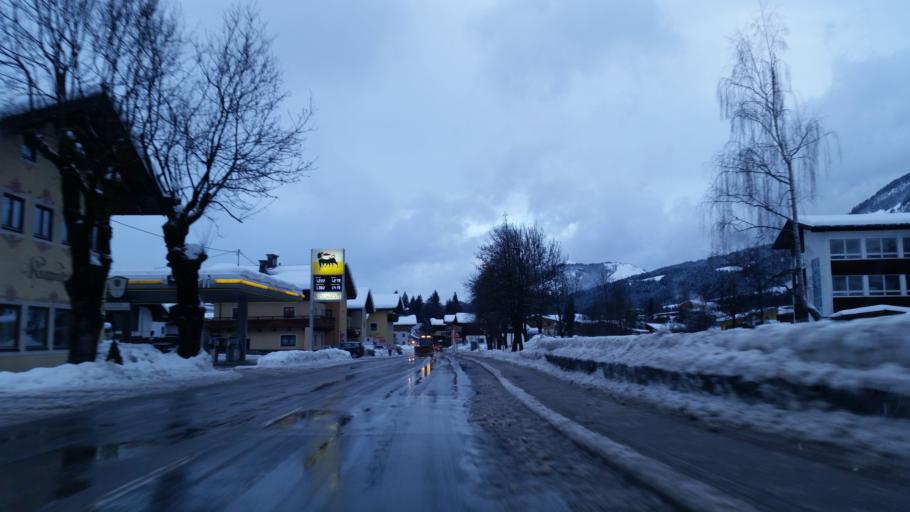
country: AT
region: Tyrol
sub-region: Politischer Bezirk Kitzbuhel
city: Fieberbrunn
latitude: 47.4796
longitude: 12.5394
